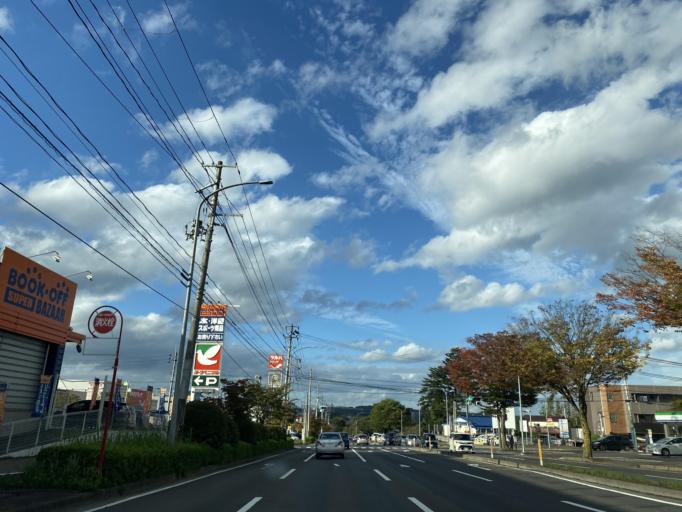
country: JP
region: Miyagi
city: Sendai-shi
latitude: 38.3189
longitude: 140.8445
